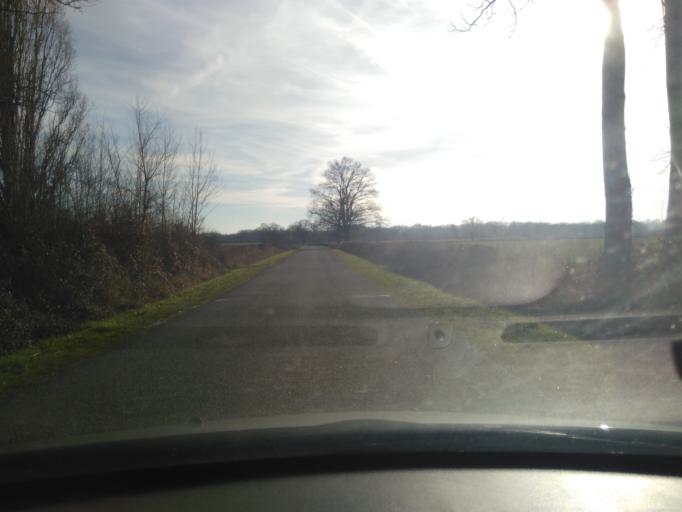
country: FR
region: Centre
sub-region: Departement du Cher
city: Orval
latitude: 46.6525
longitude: 2.4429
